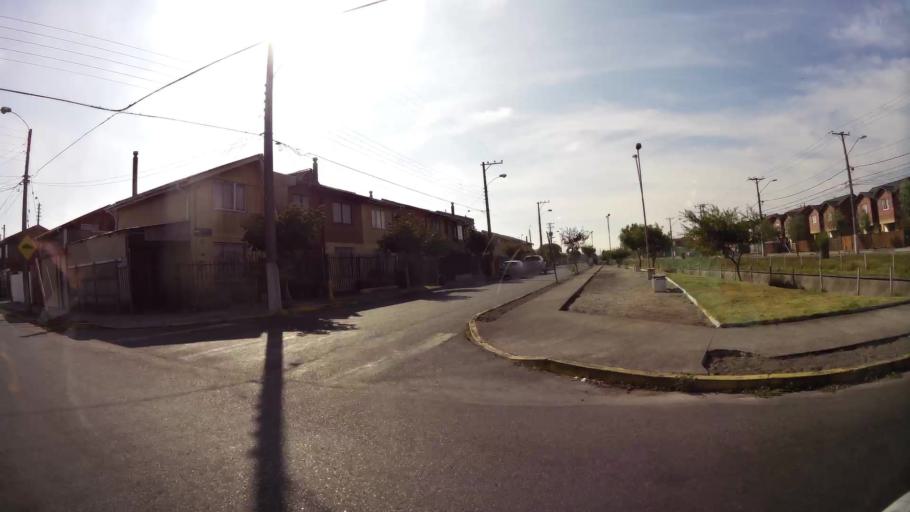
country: CL
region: Biobio
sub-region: Provincia de Concepcion
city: Talcahuano
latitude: -36.7937
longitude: -73.1145
